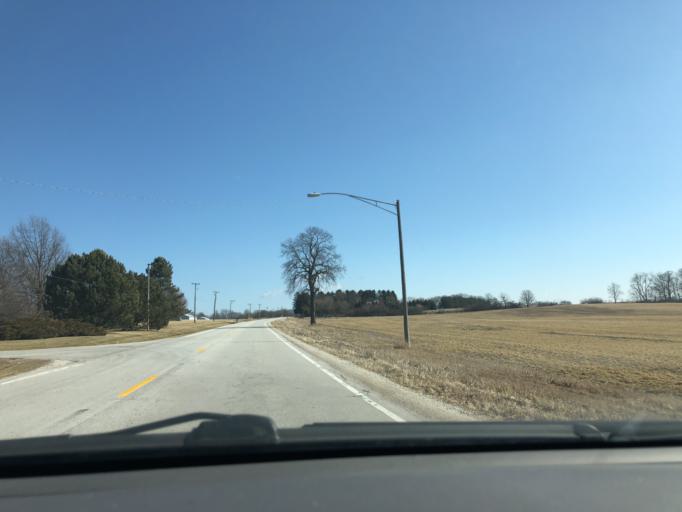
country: US
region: Illinois
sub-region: Kane County
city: Hampshire
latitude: 42.1064
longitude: -88.5005
